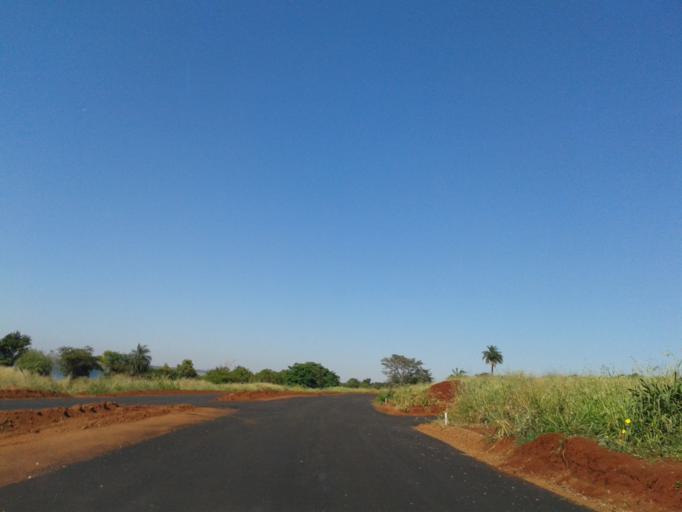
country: BR
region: Minas Gerais
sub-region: Capinopolis
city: Capinopolis
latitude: -18.5333
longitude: -49.4971
